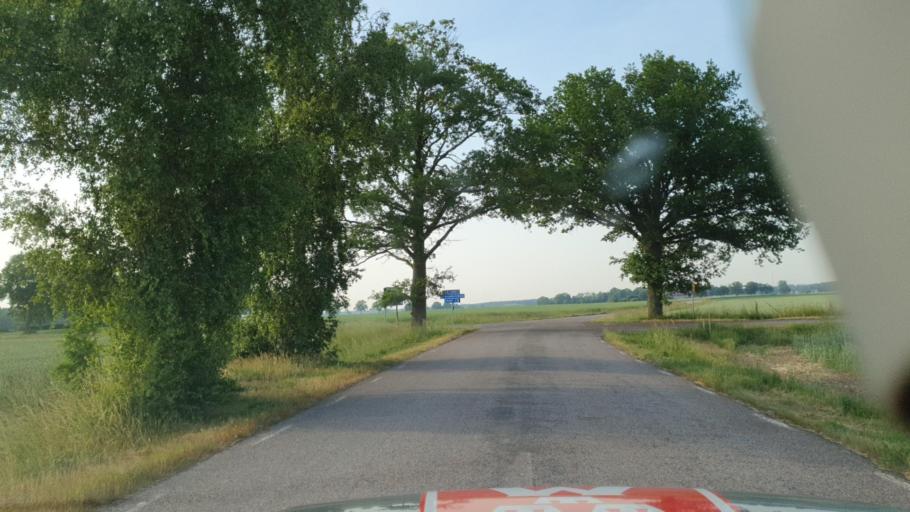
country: SE
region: Kalmar
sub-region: Kalmar Kommun
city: Ljungbyholm
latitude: 56.5610
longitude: 16.1600
